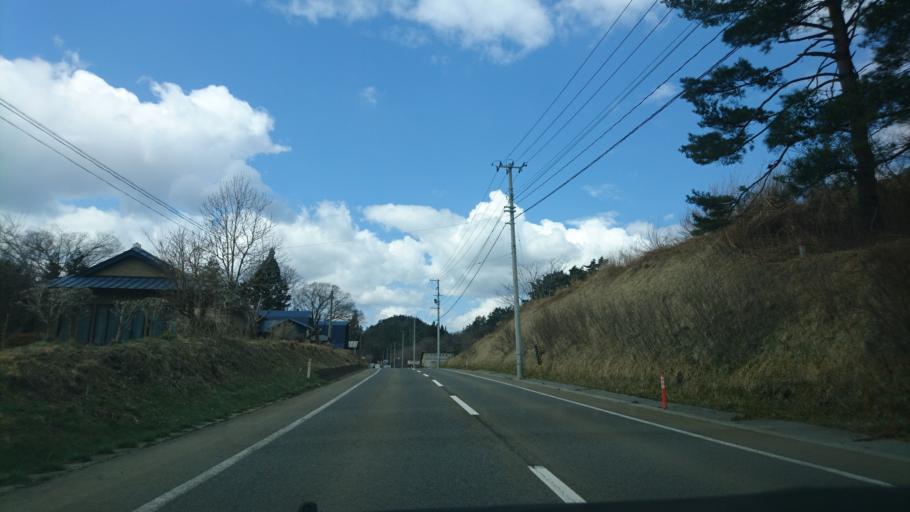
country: JP
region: Iwate
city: Tono
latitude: 39.2764
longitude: 141.4147
